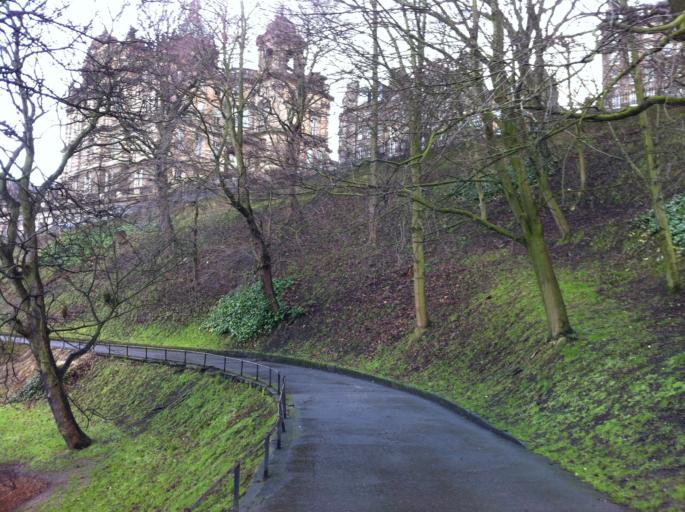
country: GB
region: Scotland
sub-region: Edinburgh
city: Edinburgh
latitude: 55.9506
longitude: -3.1948
